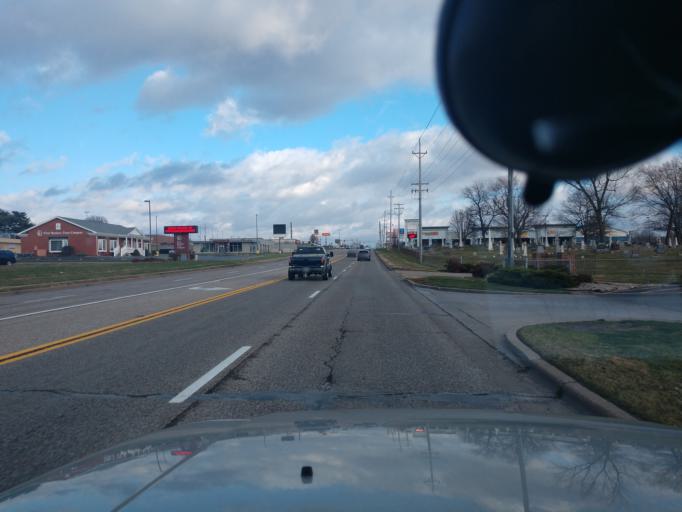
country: US
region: Illinois
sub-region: Adams County
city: Quincy
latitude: 39.9351
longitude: -91.3624
